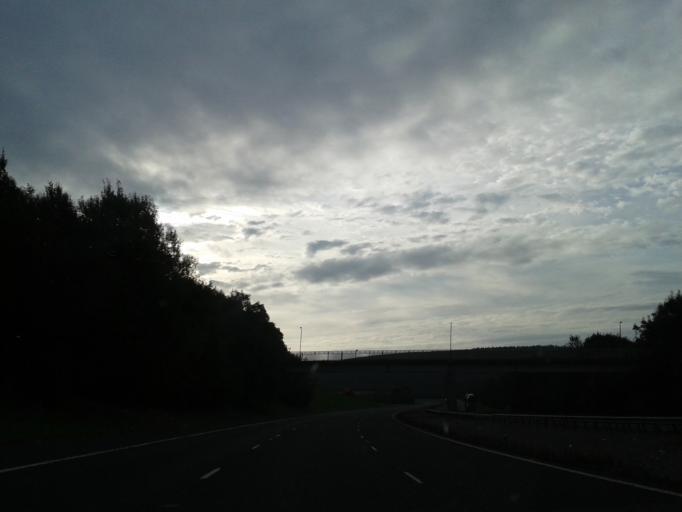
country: GB
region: Scotland
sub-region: Dumfries and Galloway
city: Annan
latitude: 55.0626
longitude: -3.2613
